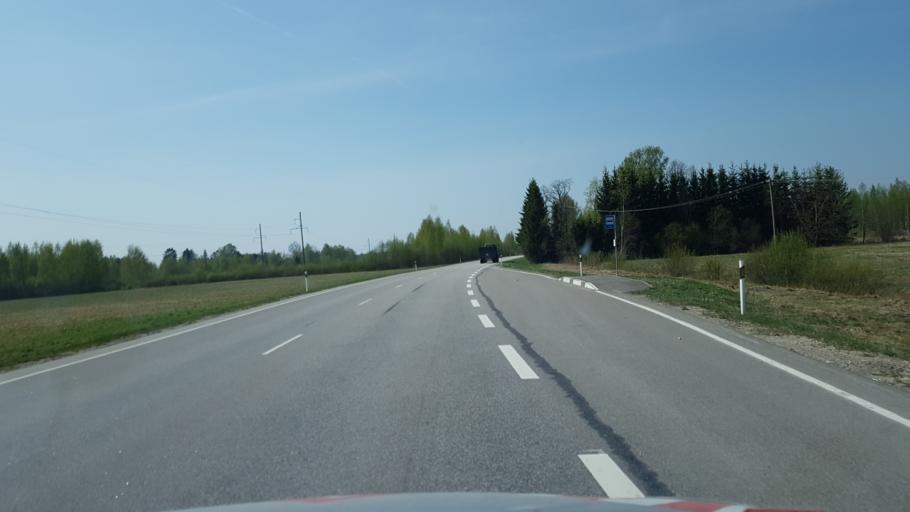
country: EE
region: Paernumaa
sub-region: Paikuse vald
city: Paikuse
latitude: 58.3947
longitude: 24.6248
